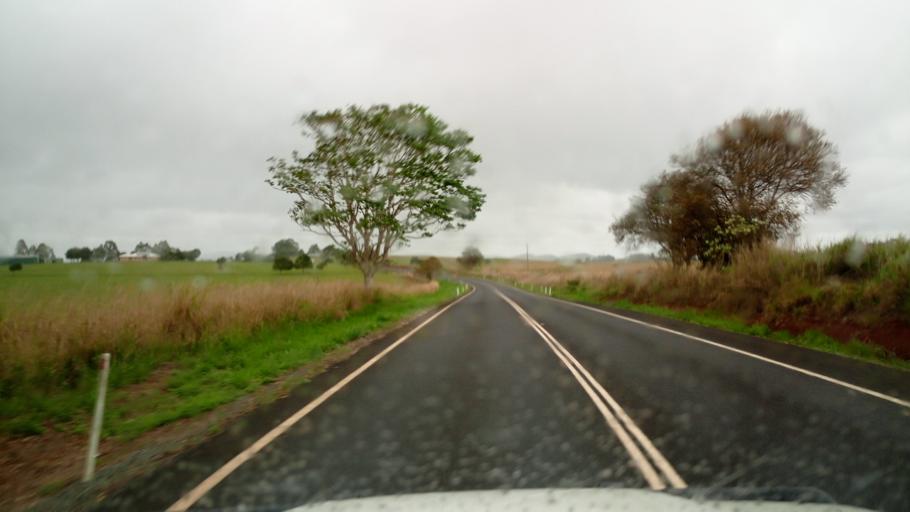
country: AU
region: Queensland
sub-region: Tablelands
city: Atherton
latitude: -17.2810
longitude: 145.6029
